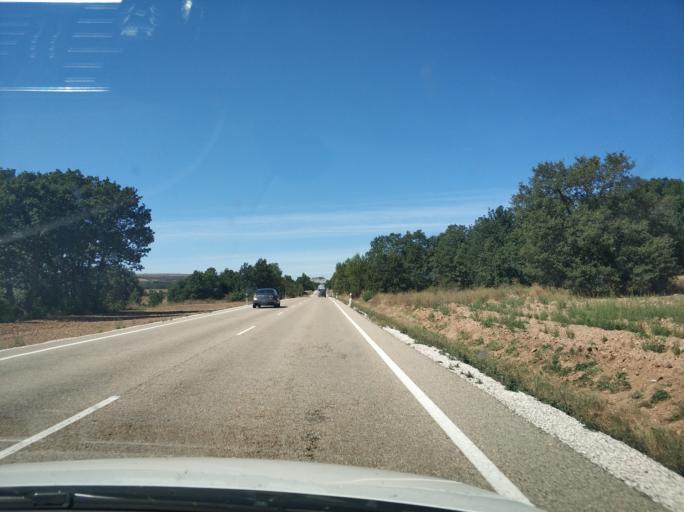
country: ES
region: Castille and Leon
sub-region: Provincia de Burgos
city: Montorio
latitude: 42.6269
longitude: -3.8510
